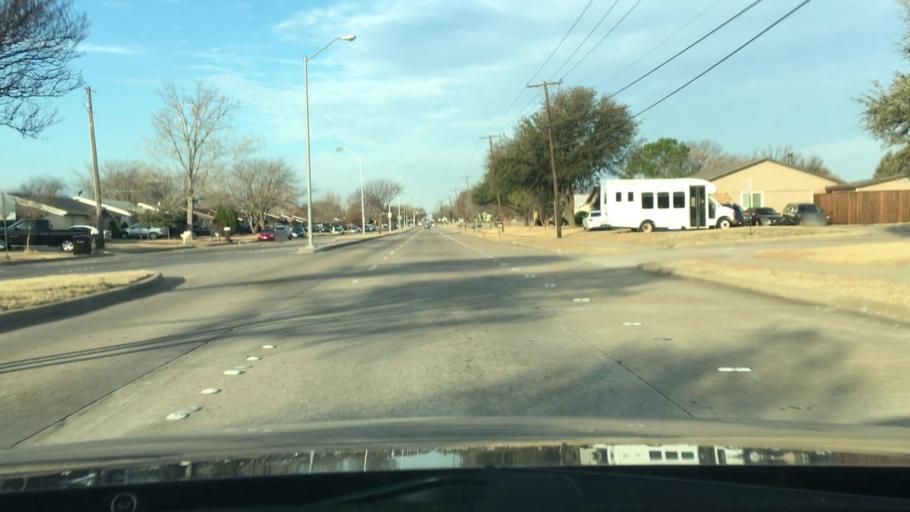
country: US
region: Texas
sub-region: Collin County
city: Plano
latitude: 33.0313
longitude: -96.6862
